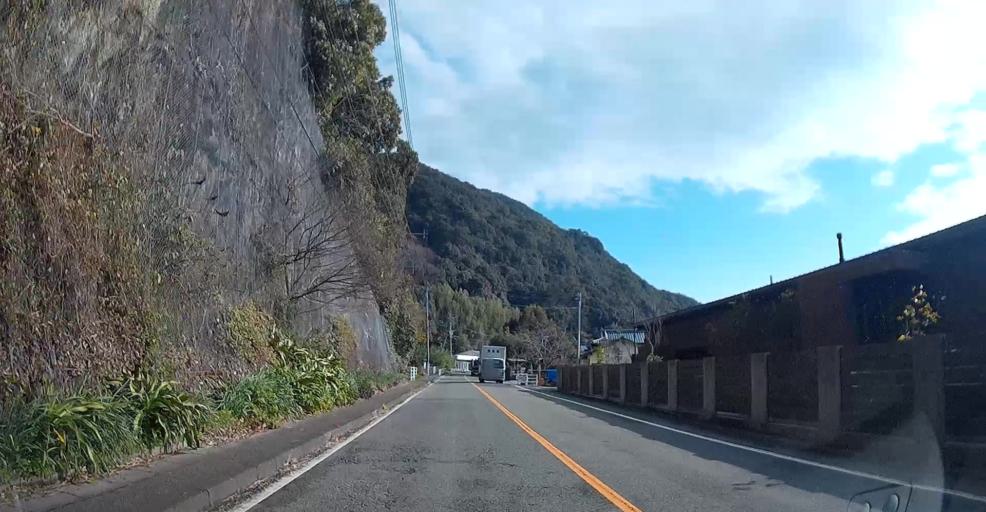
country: JP
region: Kumamoto
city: Yatsushiro
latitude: 32.6182
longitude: 130.4609
